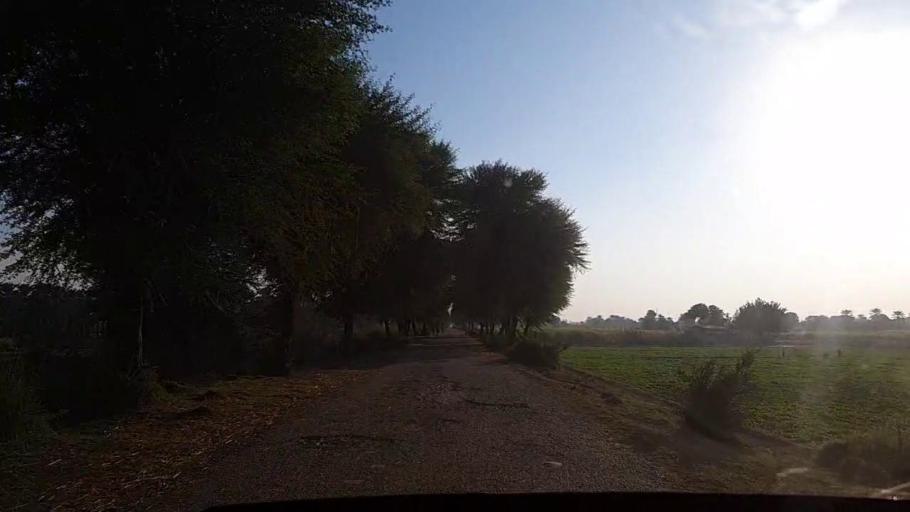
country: PK
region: Sindh
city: Sobhadero
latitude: 27.4047
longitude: 68.3914
